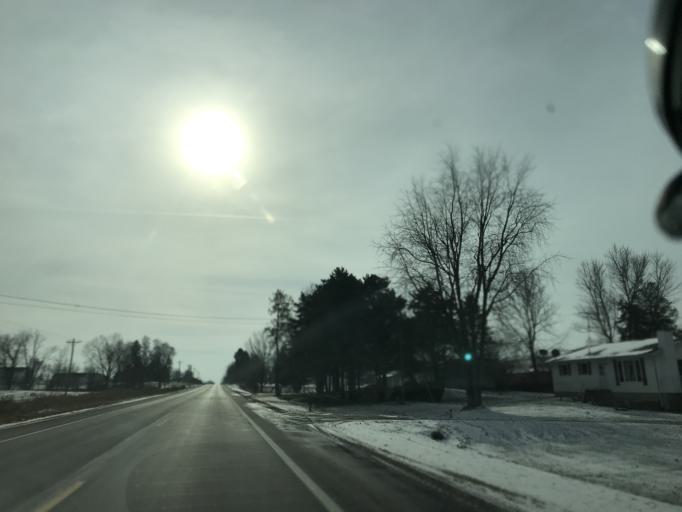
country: US
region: Michigan
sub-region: Ionia County
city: Lake Odessa
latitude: 42.7956
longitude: -85.0745
